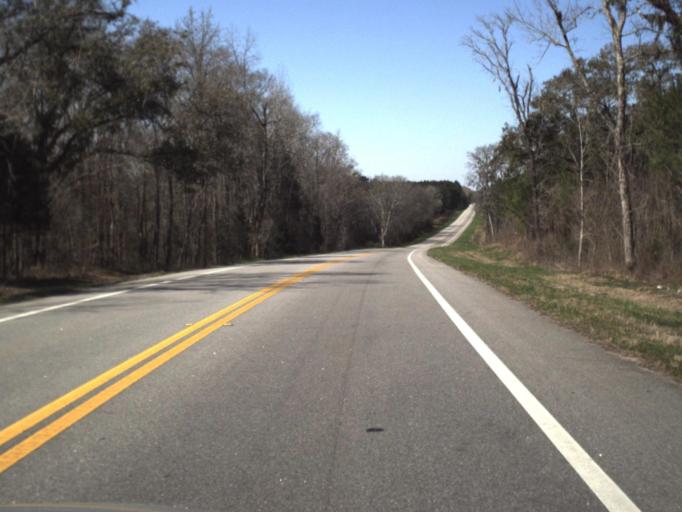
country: US
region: Florida
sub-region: Jackson County
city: Marianna
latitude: 30.8232
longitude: -85.3269
